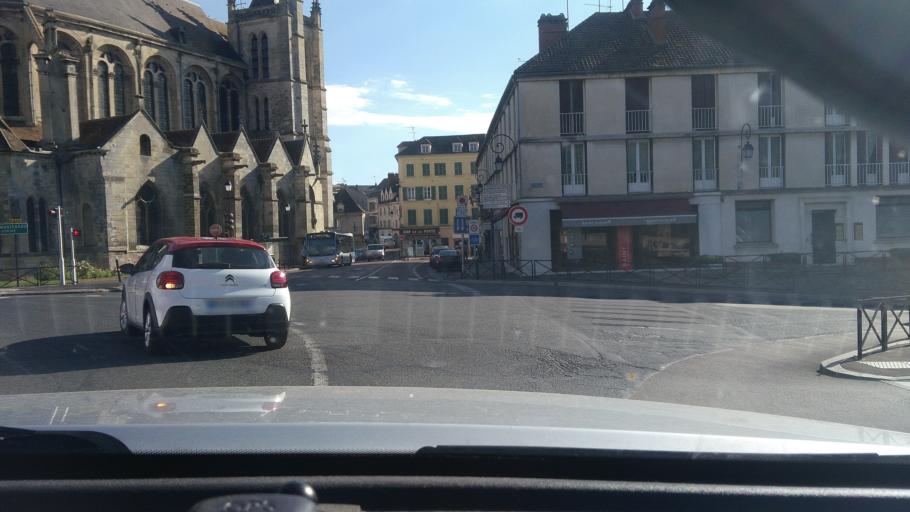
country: FR
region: Ile-de-France
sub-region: Departement de Seine-et-Marne
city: Montereau-Fault-Yonne
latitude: 48.3873
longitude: 2.9585
